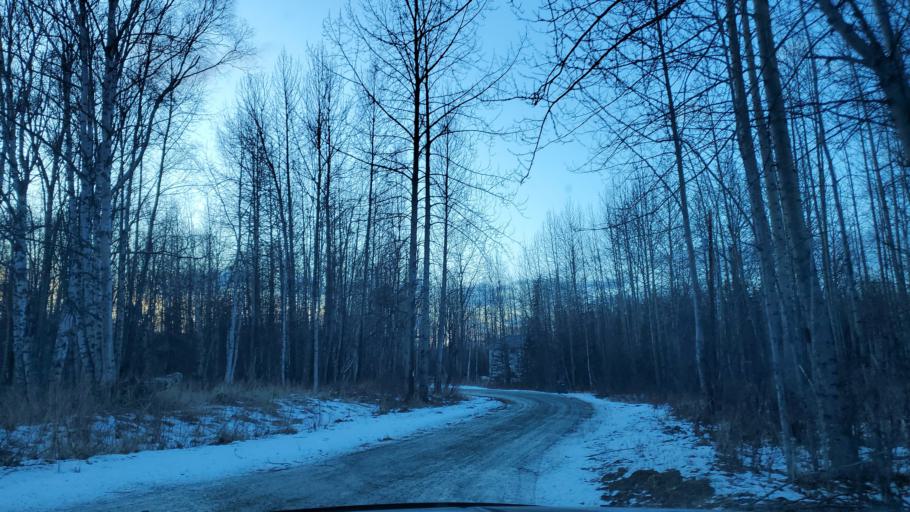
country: US
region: Alaska
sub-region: Matanuska-Susitna Borough
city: Lakes
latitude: 61.6671
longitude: -149.3307
